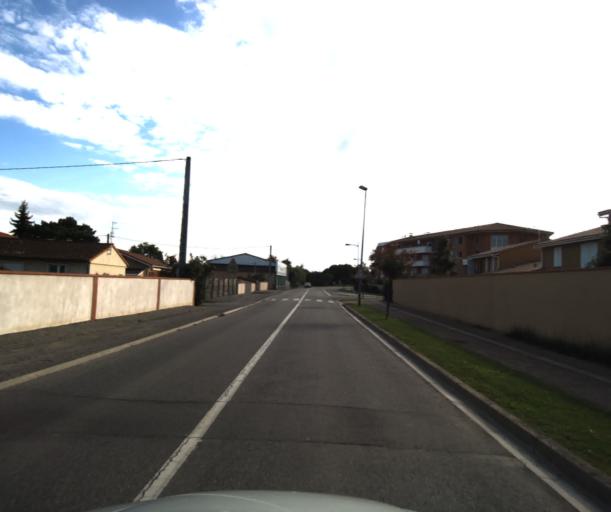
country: FR
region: Midi-Pyrenees
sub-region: Departement de la Haute-Garonne
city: Muret
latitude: 43.4603
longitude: 1.3370
